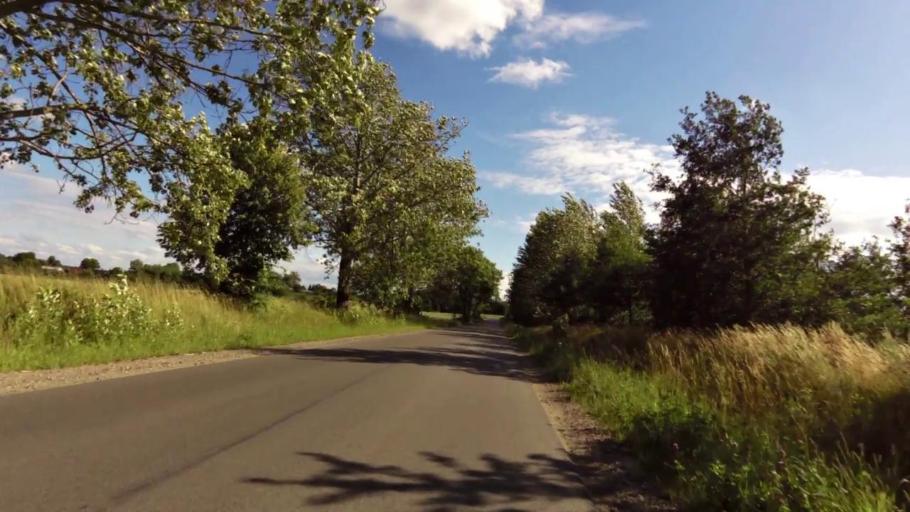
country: PL
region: West Pomeranian Voivodeship
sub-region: Powiat slawienski
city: Slawno
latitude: 54.4393
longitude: 16.7333
